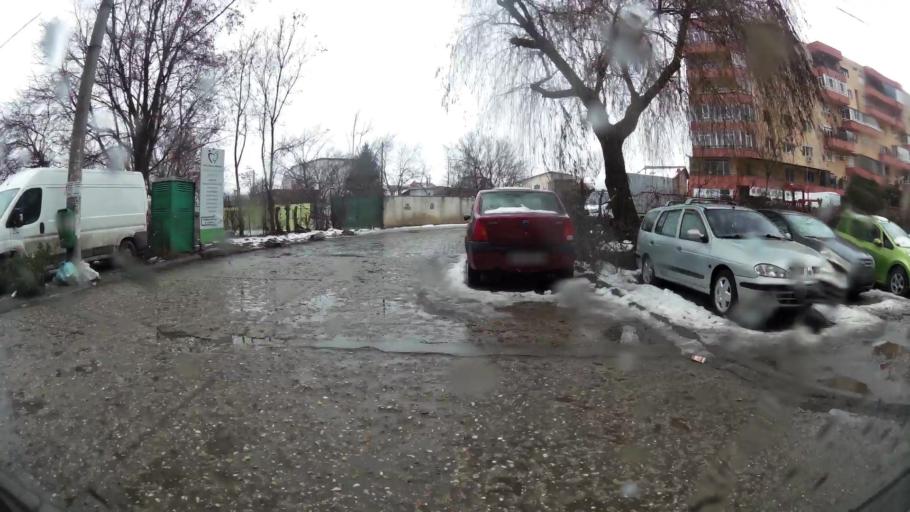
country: RO
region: Ilfov
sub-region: Comuna Chiajna
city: Rosu
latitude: 44.4124
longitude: 26.0215
